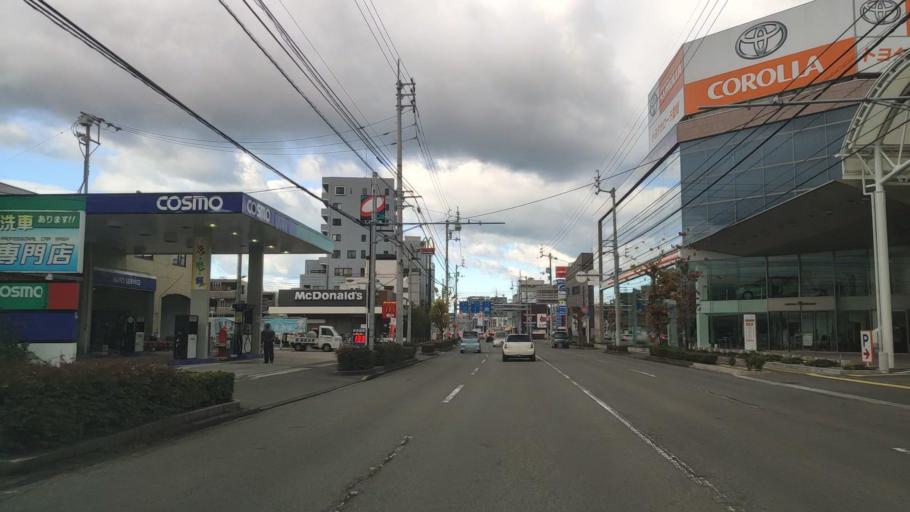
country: JP
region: Ehime
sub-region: Shikoku-chuo Shi
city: Matsuyama
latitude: 33.8546
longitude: 132.7503
